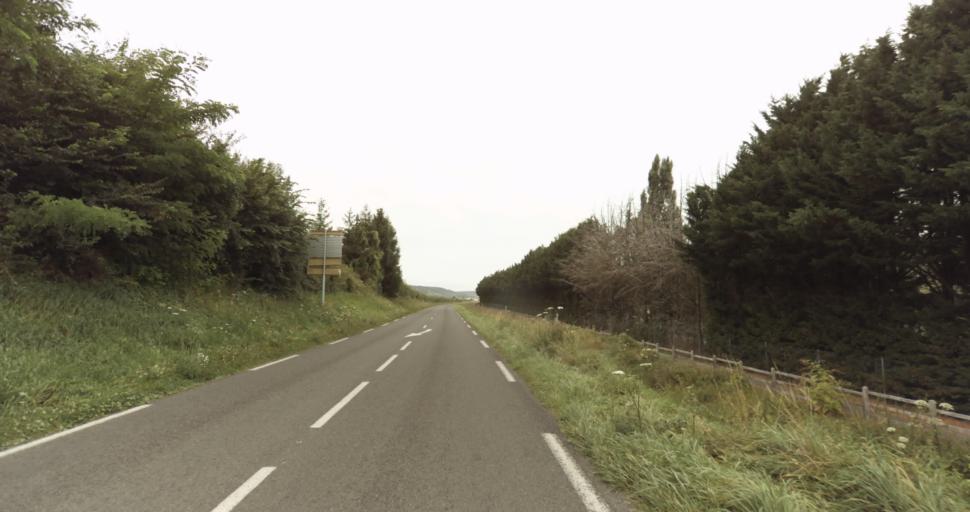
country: FR
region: Haute-Normandie
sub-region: Departement de l'Eure
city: Ivry-la-Bataille
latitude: 48.8971
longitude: 1.4553
